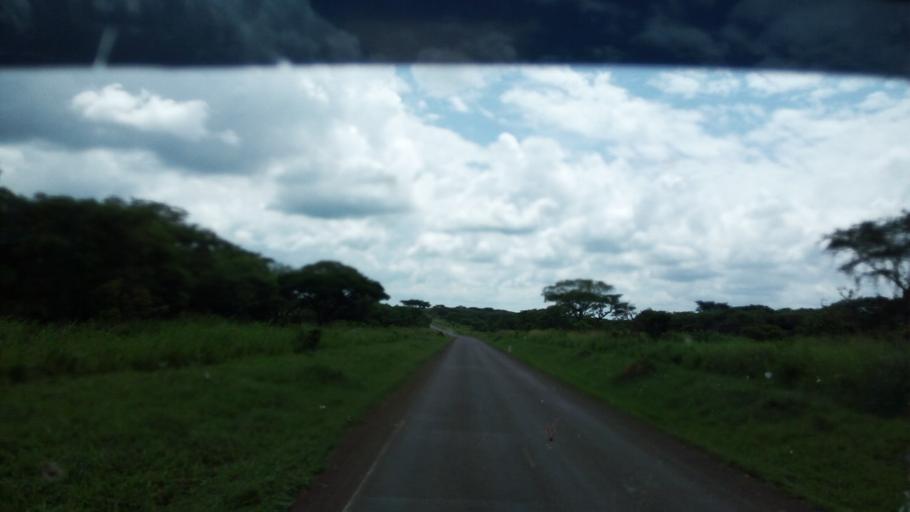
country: UG
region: Northern Region
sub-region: Oyam District
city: Oyam
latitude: 2.3027
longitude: 32.1843
